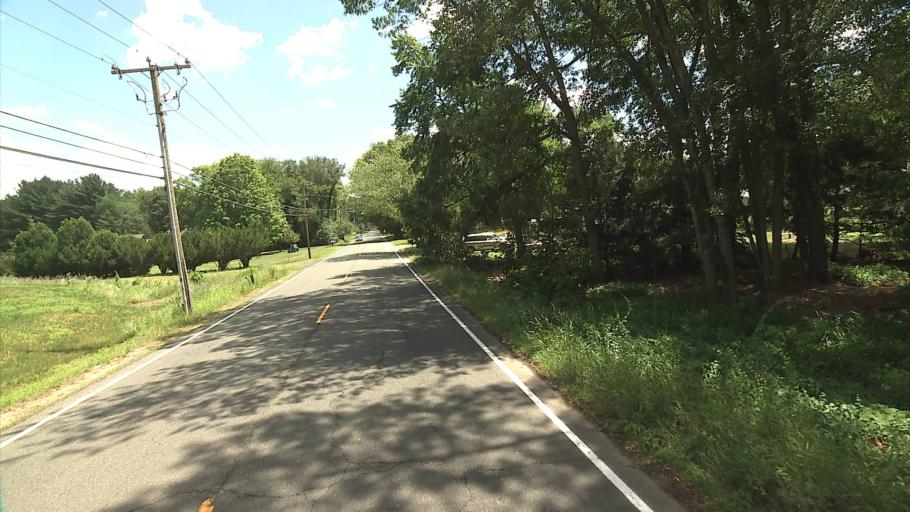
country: US
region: Connecticut
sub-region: Hartford County
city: Sherwood Manor
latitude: 42.0288
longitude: -72.5489
